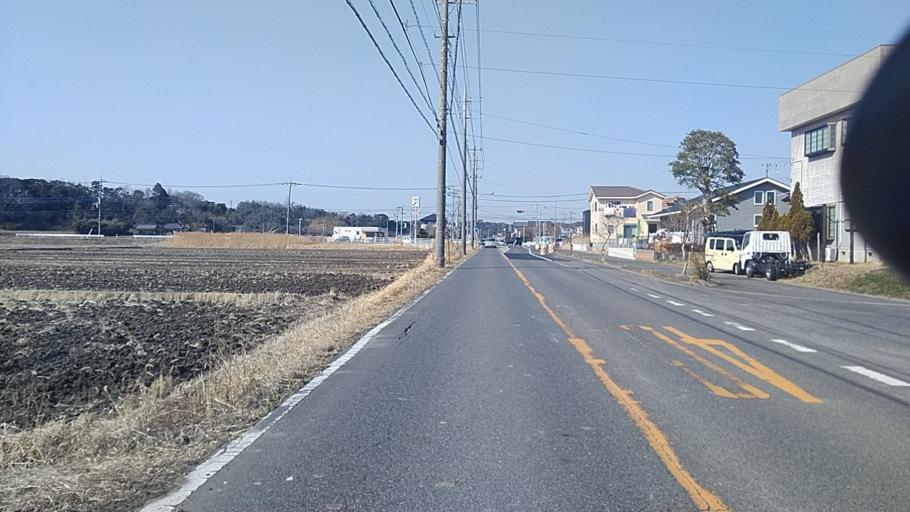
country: JP
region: Chiba
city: Mobara
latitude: 35.4529
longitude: 140.2909
